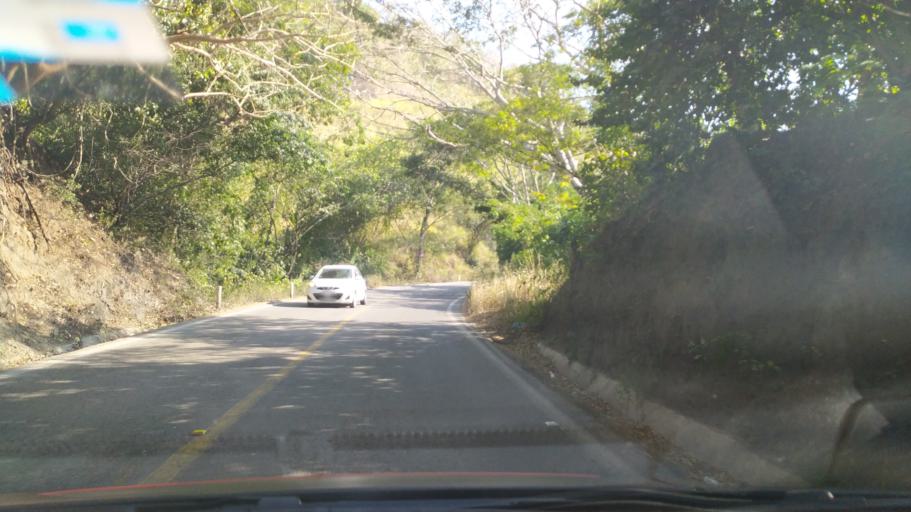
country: MX
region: Michoacan
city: Coahuayana Viejo
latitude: 18.6172
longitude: -103.6781
